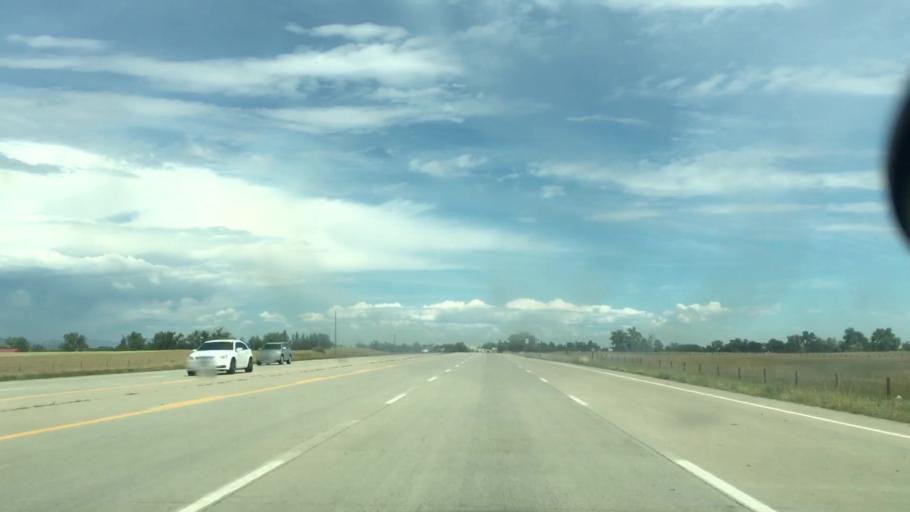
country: US
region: Colorado
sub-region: Boulder County
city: Longmont
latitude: 40.2213
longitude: -105.1023
